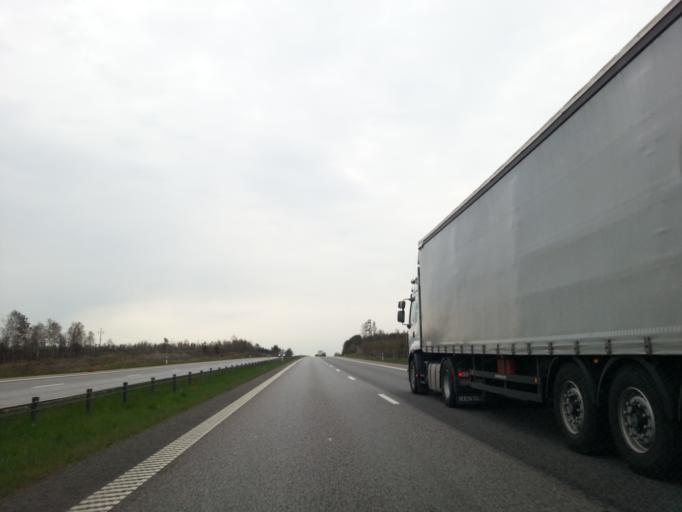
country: SE
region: Halland
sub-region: Halmstads Kommun
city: Aled
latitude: 56.7308
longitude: 12.8783
